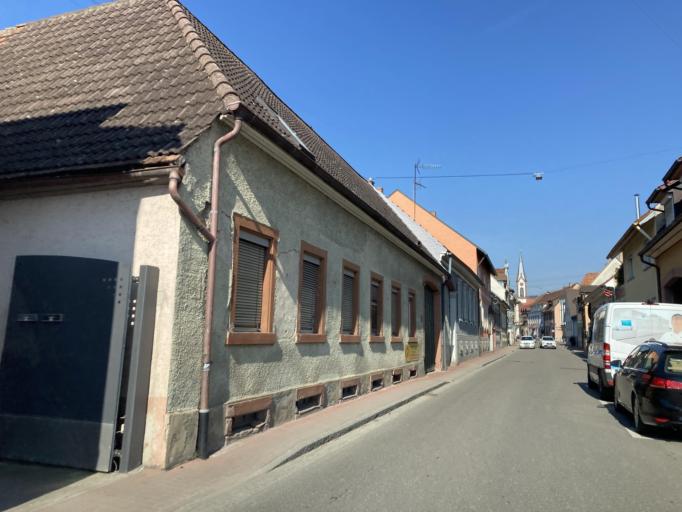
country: DE
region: Baden-Wuerttemberg
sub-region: Freiburg Region
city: Ihringen
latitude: 48.0419
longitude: 7.6477
